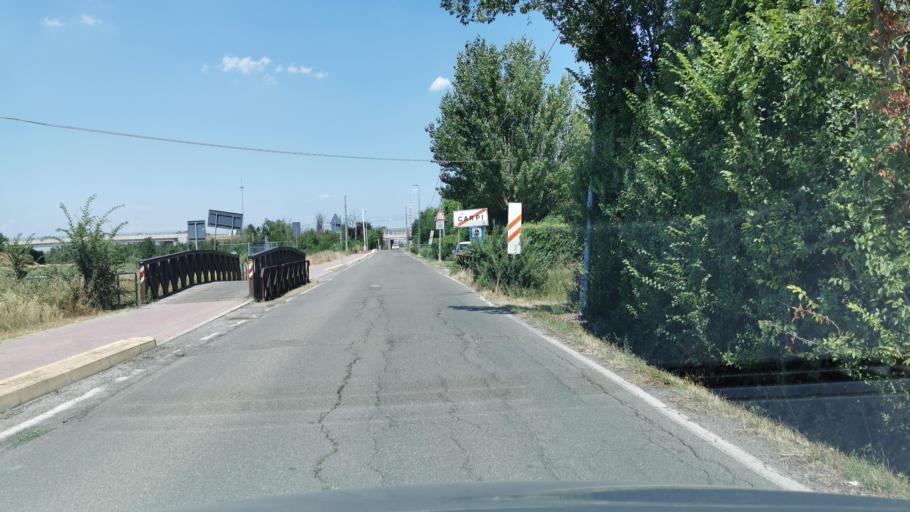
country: IT
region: Emilia-Romagna
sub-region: Provincia di Modena
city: Fossoli
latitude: 44.8042
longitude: 10.8862
